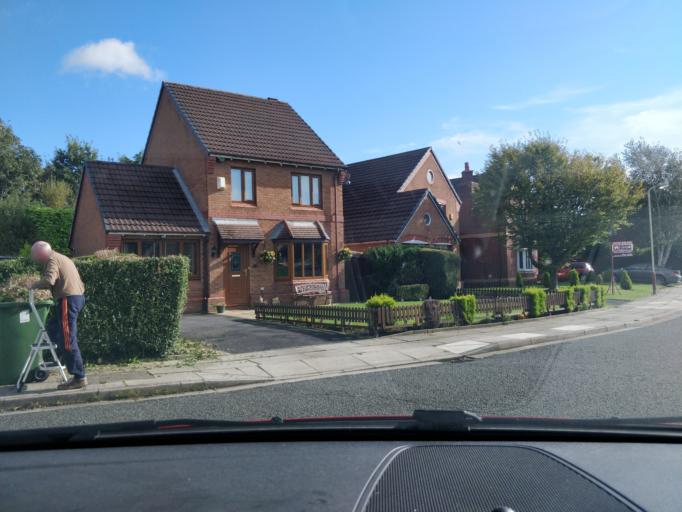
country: GB
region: England
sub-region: Sefton
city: Southport
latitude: 53.6304
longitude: -2.9716
